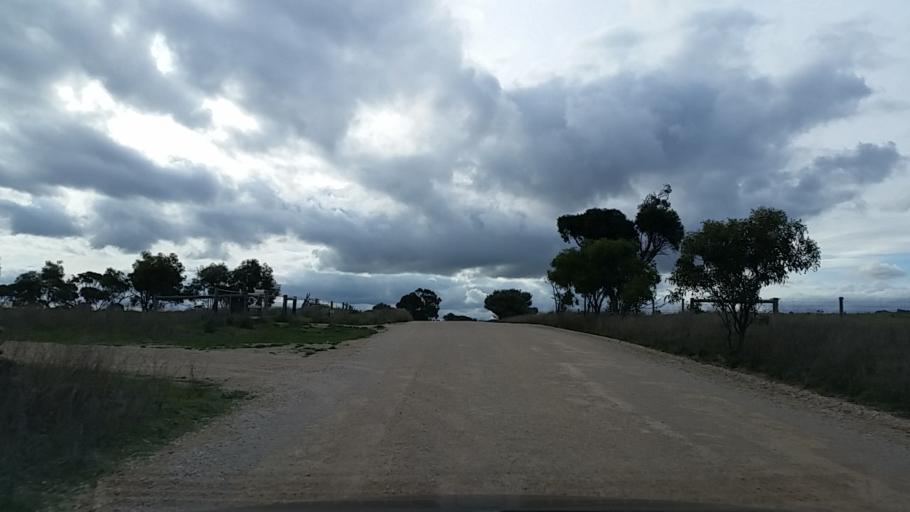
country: AU
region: South Australia
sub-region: Mount Barker
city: Callington
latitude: -35.0078
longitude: 139.0625
